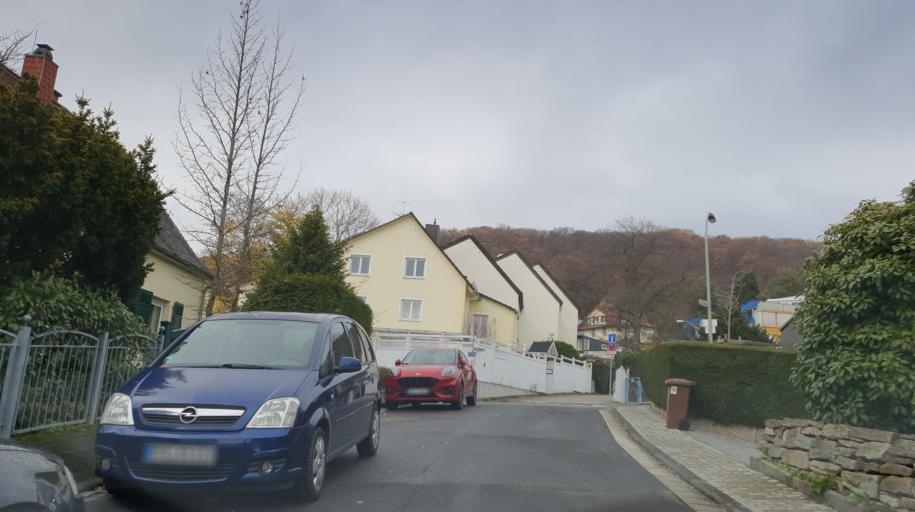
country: DE
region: Hesse
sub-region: Regierungsbezirk Darmstadt
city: Hofheim am Taunus
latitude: 50.0912
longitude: 8.4393
